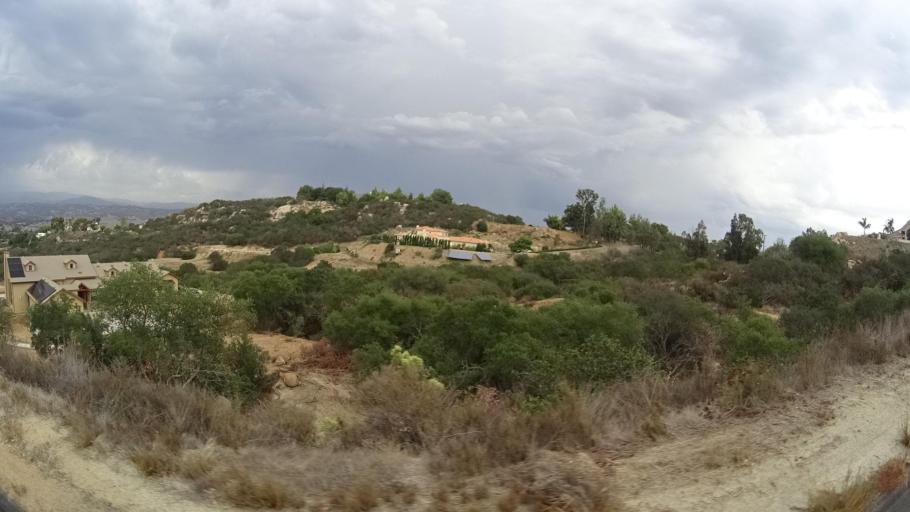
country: US
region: California
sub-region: San Diego County
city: San Pasqual
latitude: 33.0200
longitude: -116.9539
